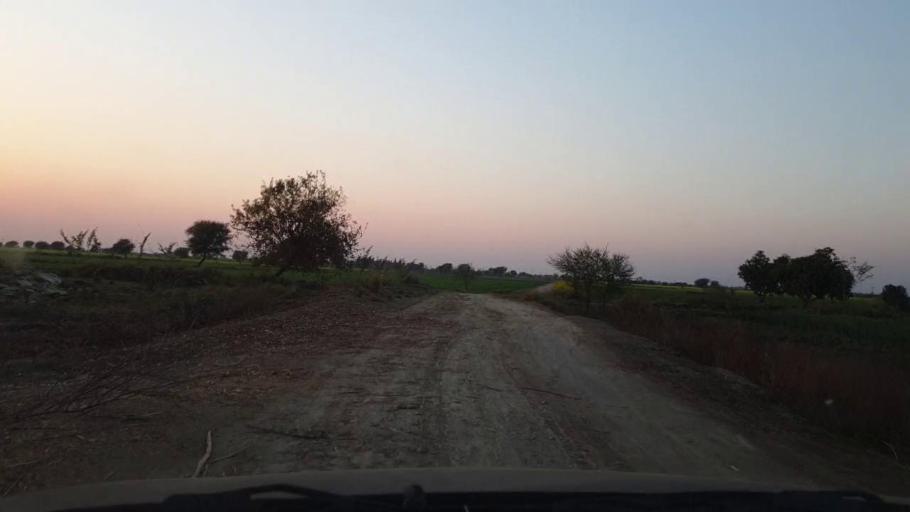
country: PK
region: Sindh
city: Jhol
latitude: 25.9393
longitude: 68.9552
